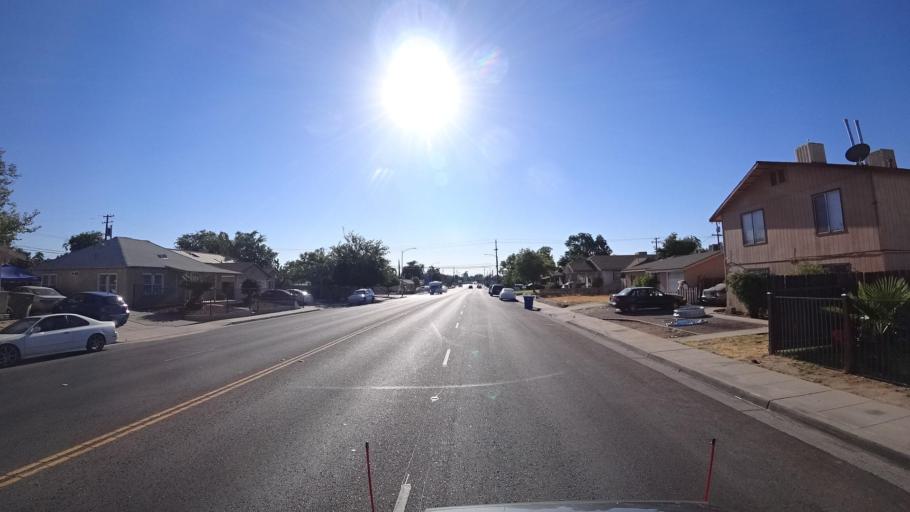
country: US
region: California
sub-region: Fresno County
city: Fresno
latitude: 36.7722
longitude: -119.7960
